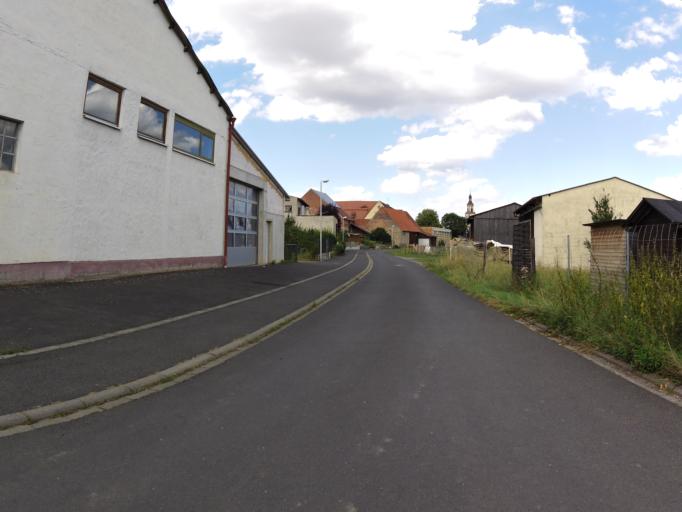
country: DE
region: Bavaria
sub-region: Regierungsbezirk Unterfranken
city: Bergrheinfeld
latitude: 50.0031
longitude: 10.1787
